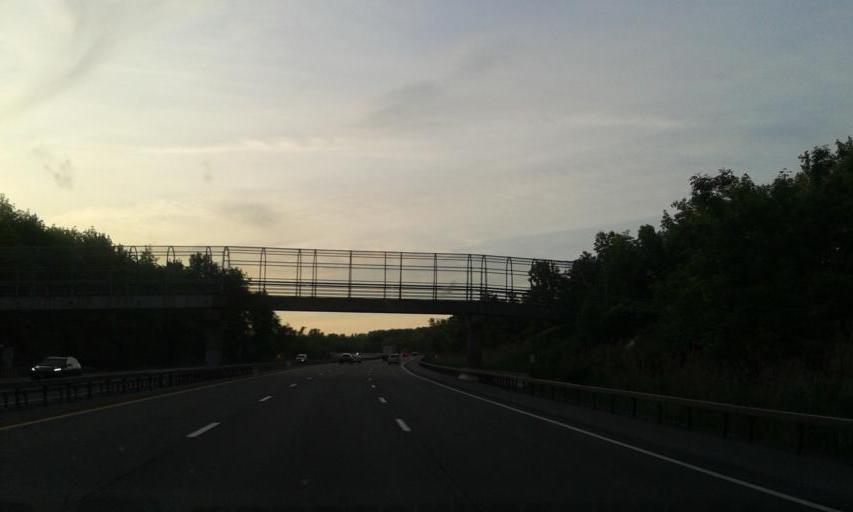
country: US
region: New York
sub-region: Onondaga County
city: Lakeland
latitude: 43.0999
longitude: -76.2421
